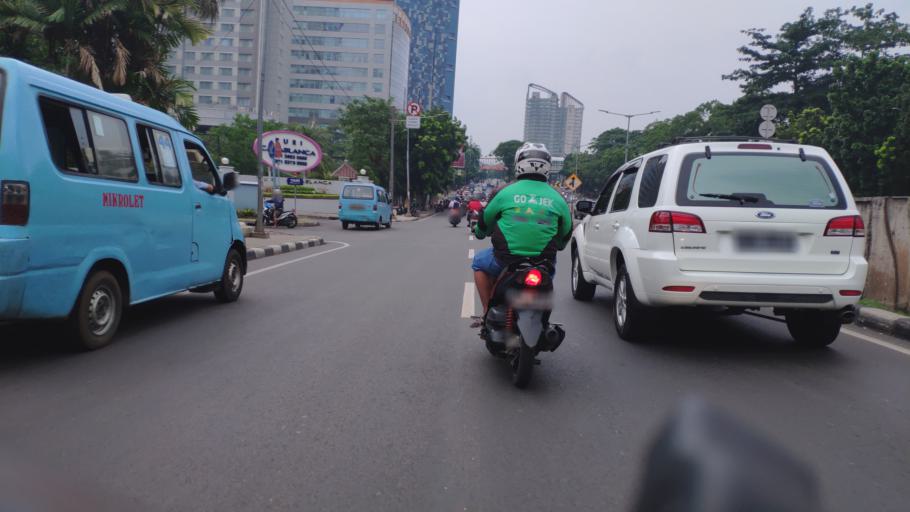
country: ID
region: Jakarta Raya
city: Jakarta
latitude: -6.2251
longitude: 106.8385
